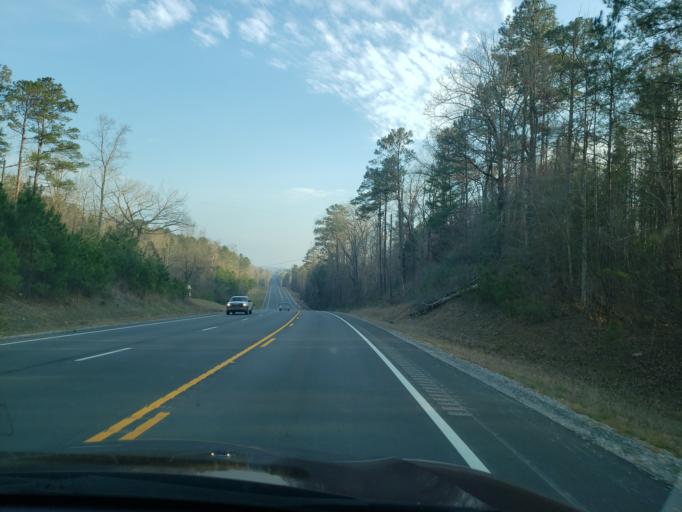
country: US
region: Alabama
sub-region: Hale County
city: Moundville
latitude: 32.8567
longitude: -87.6136
